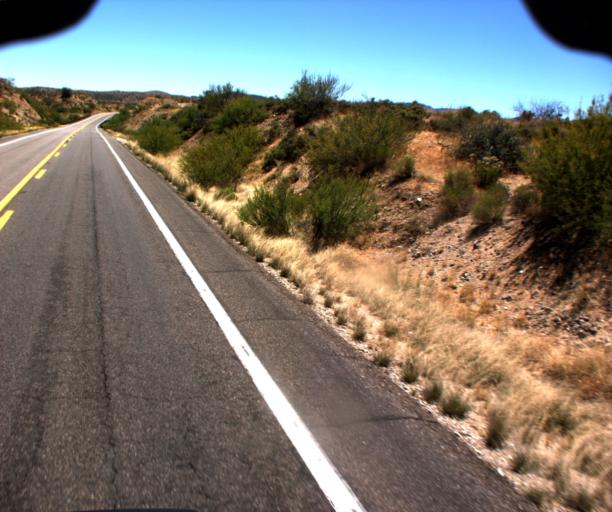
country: US
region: Arizona
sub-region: Gila County
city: Globe
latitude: 33.3453
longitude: -110.7301
